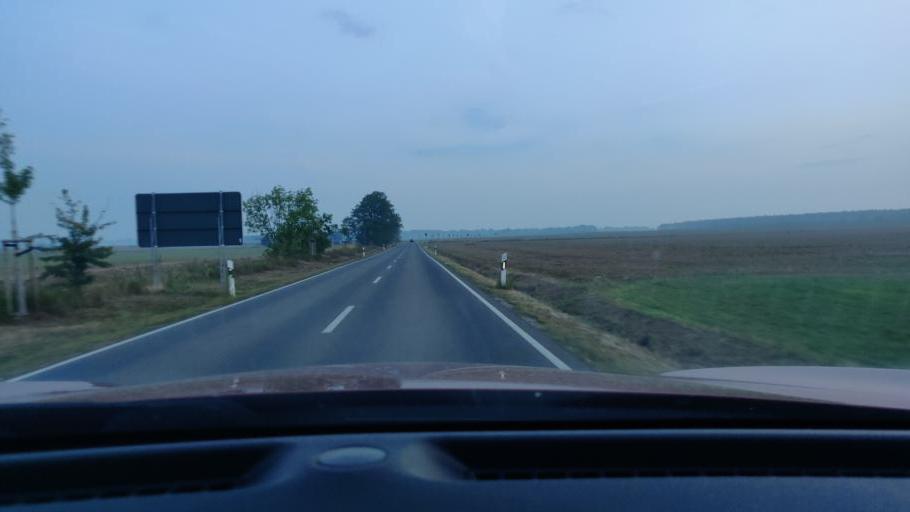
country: DE
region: Saxony
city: Schildau
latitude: 51.4965
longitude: 12.9130
